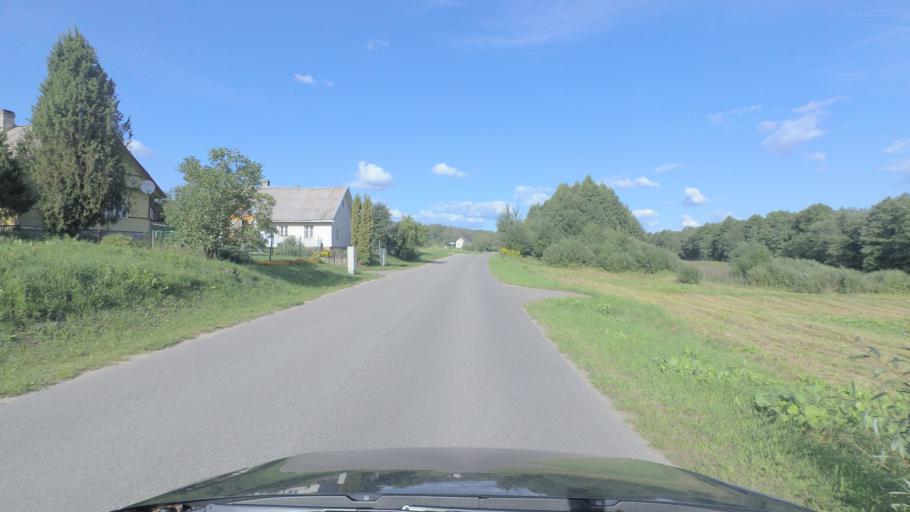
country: LT
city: Nemencine
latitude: 54.8600
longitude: 25.3900
